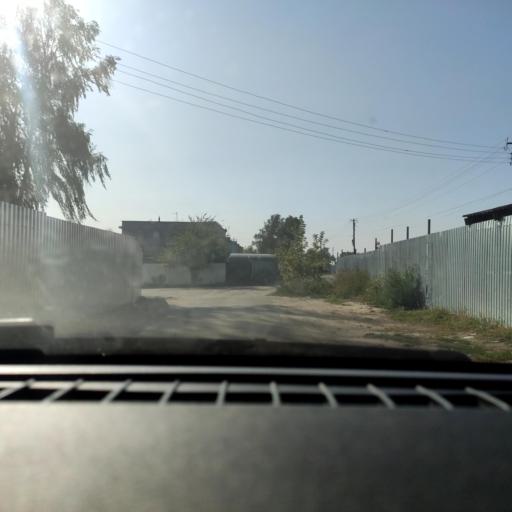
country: RU
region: Voronezj
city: Maslovka
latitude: 51.5449
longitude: 39.2192
